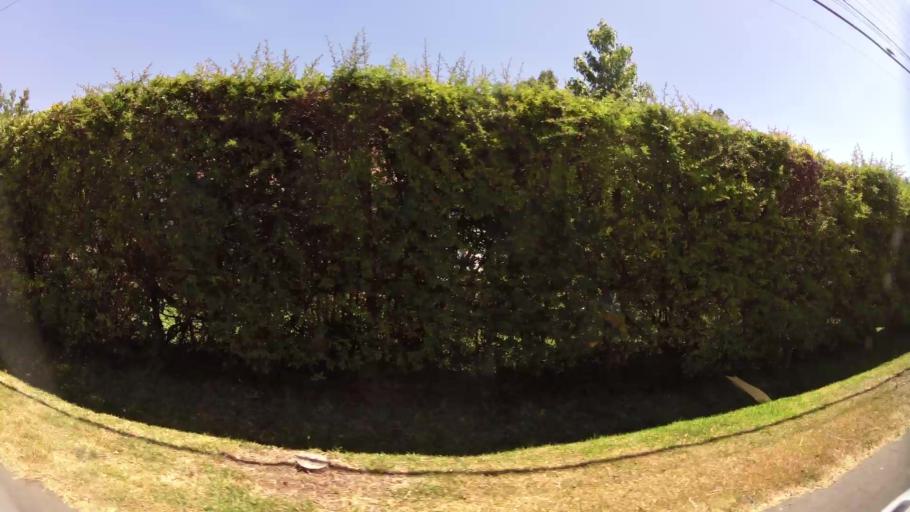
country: CL
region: Maule
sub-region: Provincia de Curico
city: Curico
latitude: -34.9970
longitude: -71.2132
